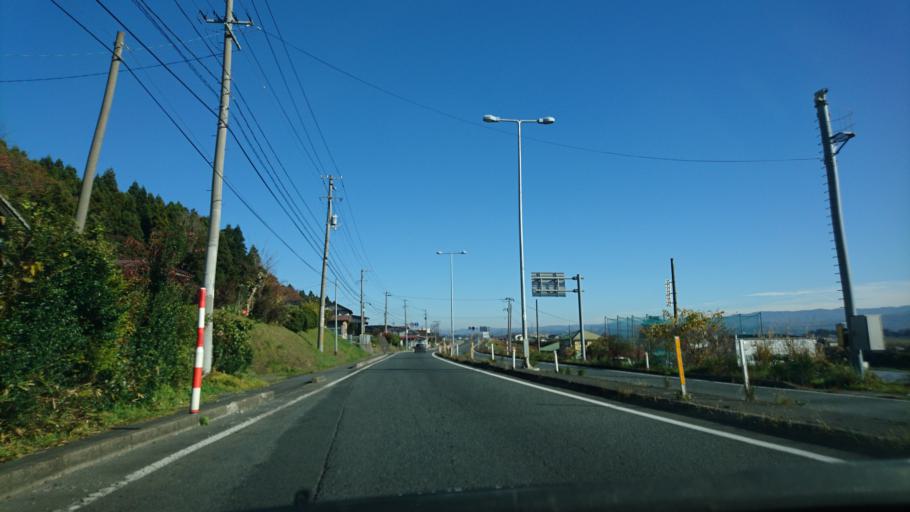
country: JP
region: Iwate
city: Mizusawa
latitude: 39.0742
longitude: 141.1317
